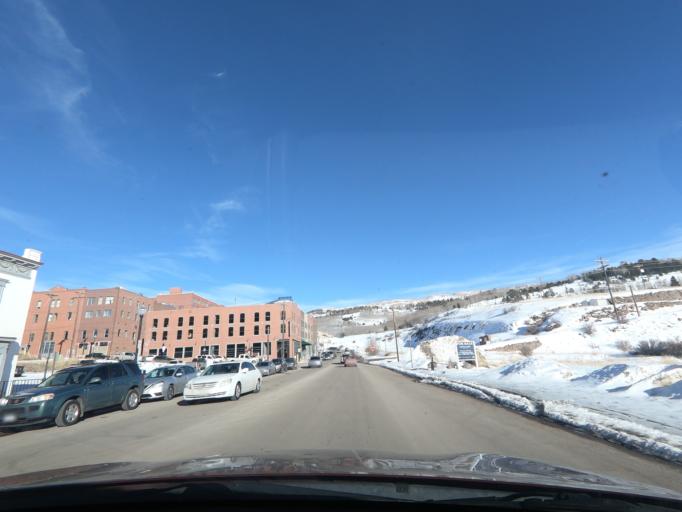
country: US
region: Colorado
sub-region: Teller County
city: Cripple Creek
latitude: 38.7458
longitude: -105.1752
